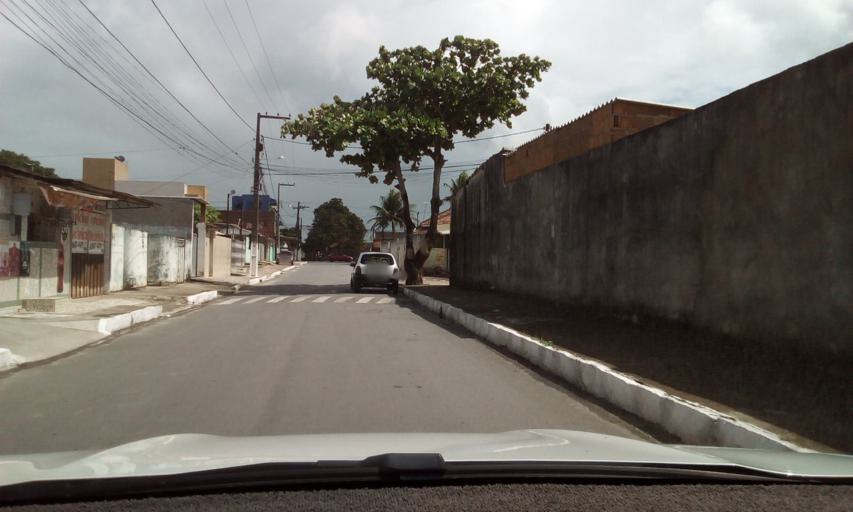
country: BR
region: Paraiba
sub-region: Santa Rita
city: Santa Rita
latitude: -7.1425
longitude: -34.9671
